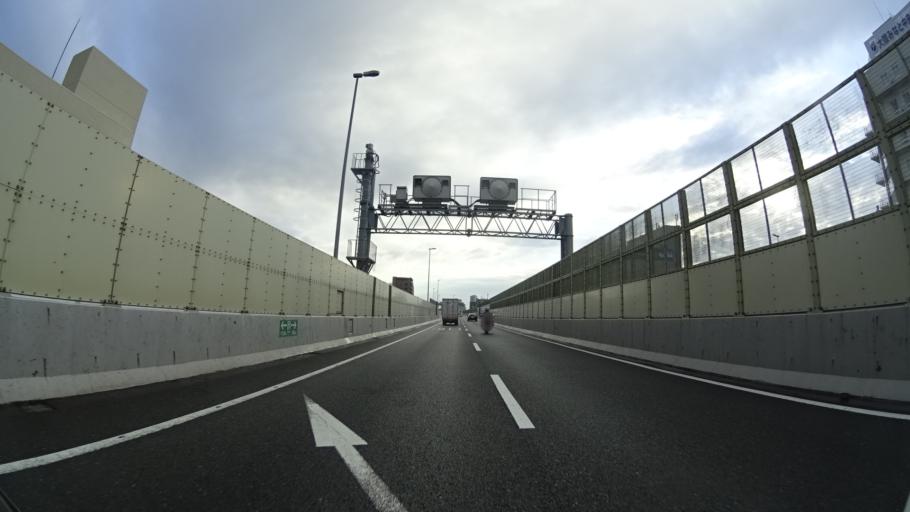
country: JP
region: Osaka
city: Osaka-shi
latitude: 34.6684
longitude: 135.4615
